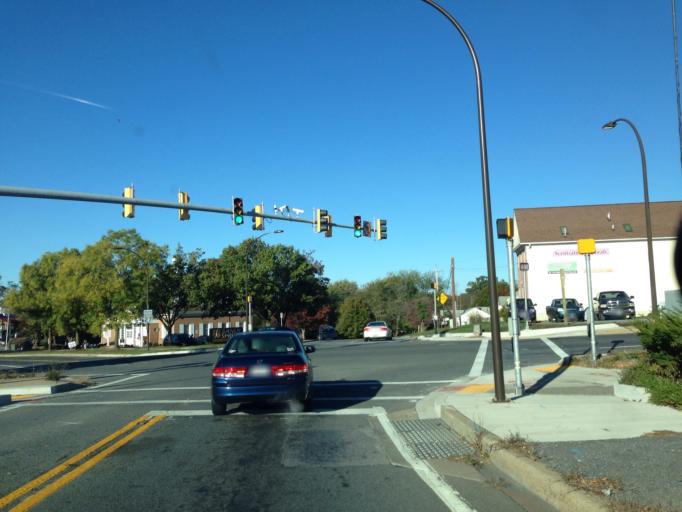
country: US
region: Maryland
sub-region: Montgomery County
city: Damascus
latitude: 39.2885
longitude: -77.2057
